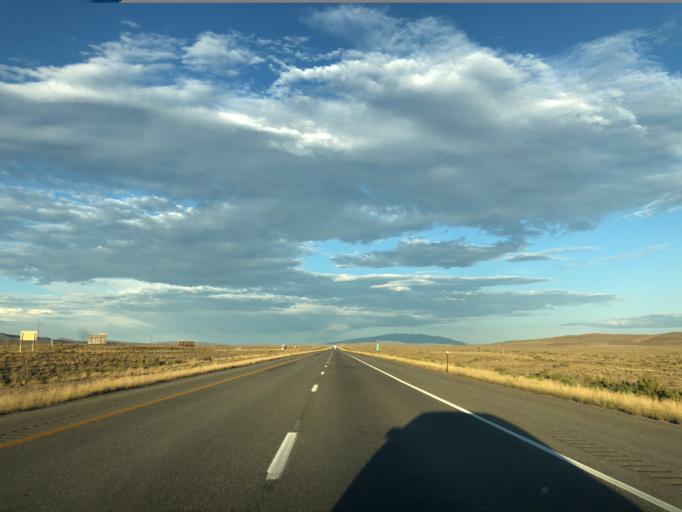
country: US
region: Wyoming
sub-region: Carbon County
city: Rawlins
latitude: 41.7654
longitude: -107.0260
